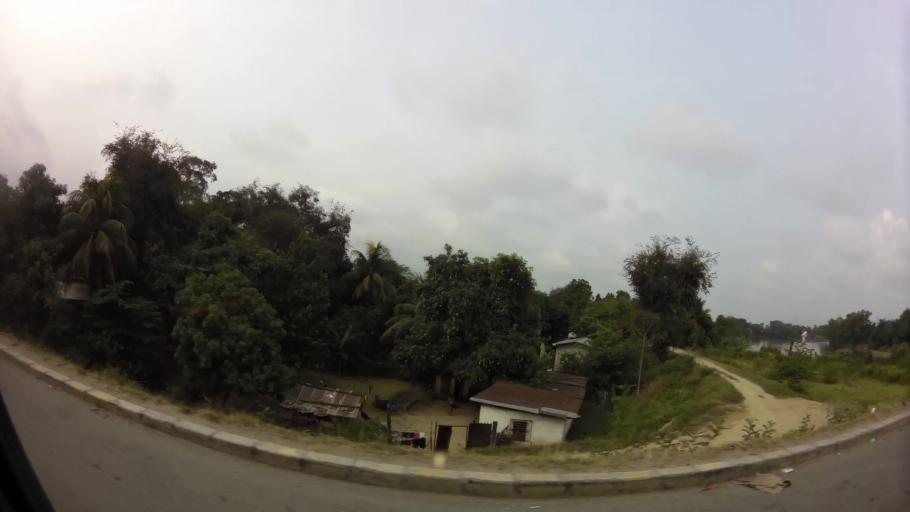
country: HN
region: Yoro
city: El Progreso
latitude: 15.4035
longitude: -87.8188
